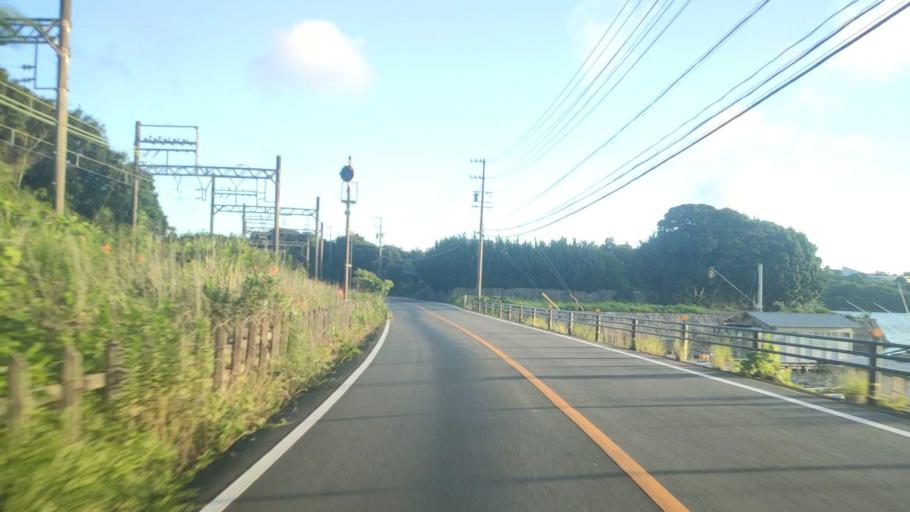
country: JP
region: Mie
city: Toba
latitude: 34.3132
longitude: 136.8253
